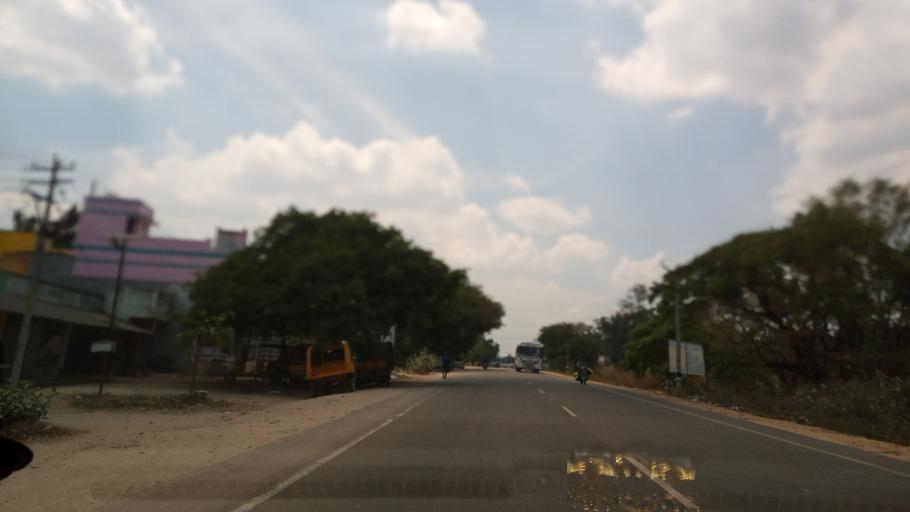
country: IN
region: Tamil Nadu
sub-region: Vellore
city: Walajapet
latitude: 12.9212
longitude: 79.3785
